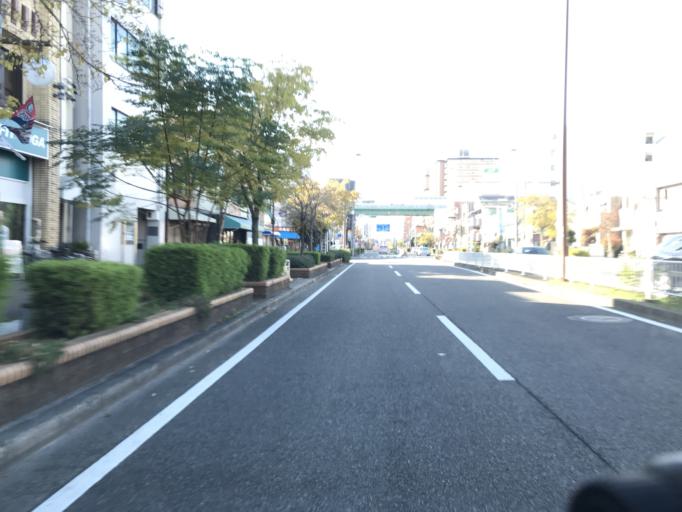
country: JP
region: Aichi
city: Nagoya-shi
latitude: 35.1923
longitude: 136.8935
